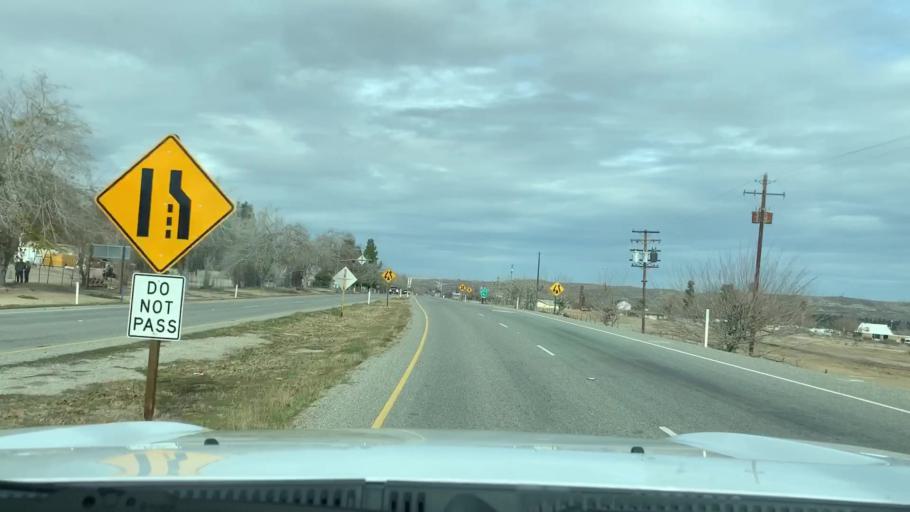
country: US
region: California
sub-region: Kern County
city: South Taft
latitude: 35.1382
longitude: -119.4471
